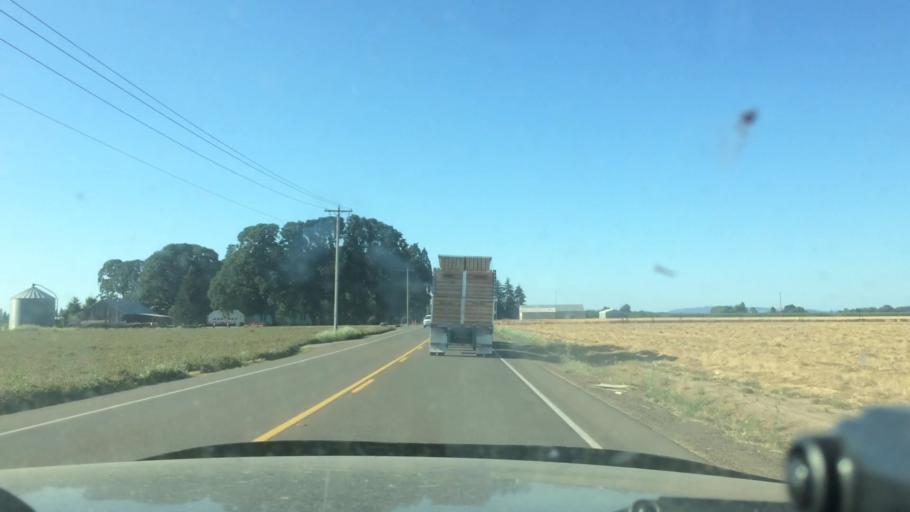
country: US
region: Oregon
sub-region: Marion County
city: Gervais
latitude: 45.0829
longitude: -122.9764
